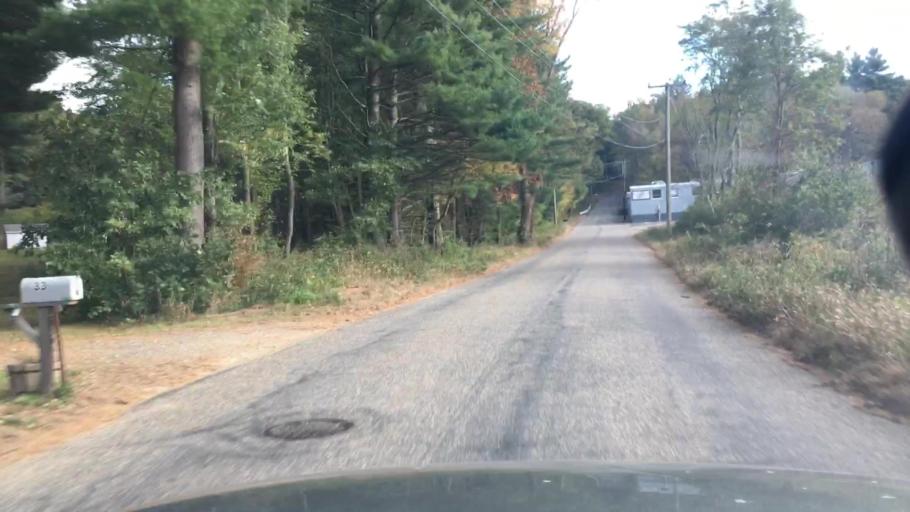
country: US
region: Connecticut
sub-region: Tolland County
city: Stafford
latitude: 41.9697
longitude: -72.2881
